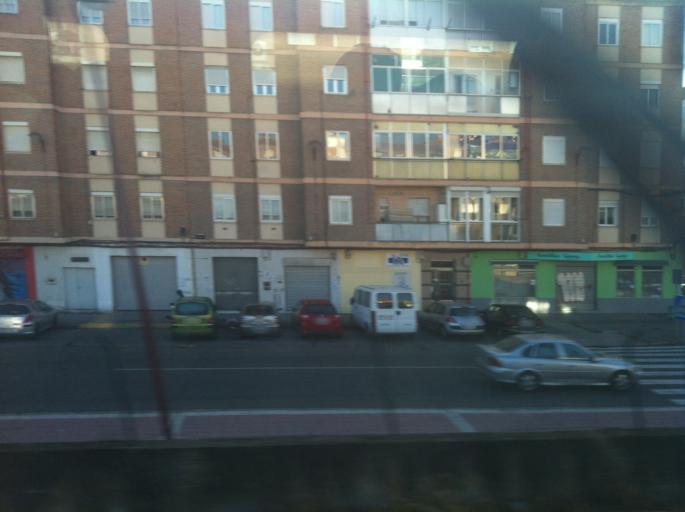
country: ES
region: Castille and Leon
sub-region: Provincia de Valladolid
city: Valladolid
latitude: 41.6506
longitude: -4.7103
